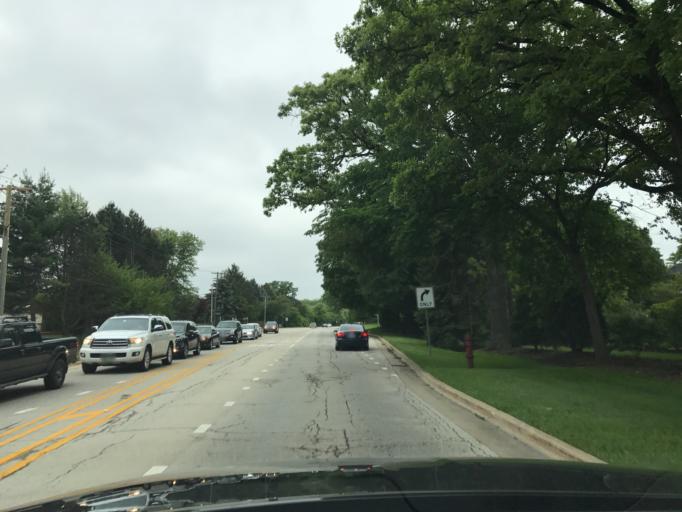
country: US
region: Illinois
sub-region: DuPage County
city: Woodridge
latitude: 41.7582
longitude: -88.0763
